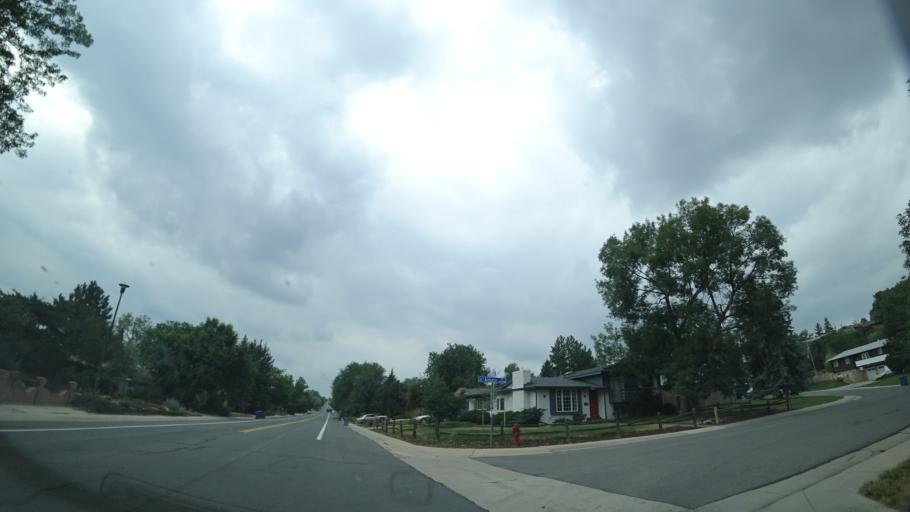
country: US
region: Colorado
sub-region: Jefferson County
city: West Pleasant View
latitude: 39.7050
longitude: -105.1478
